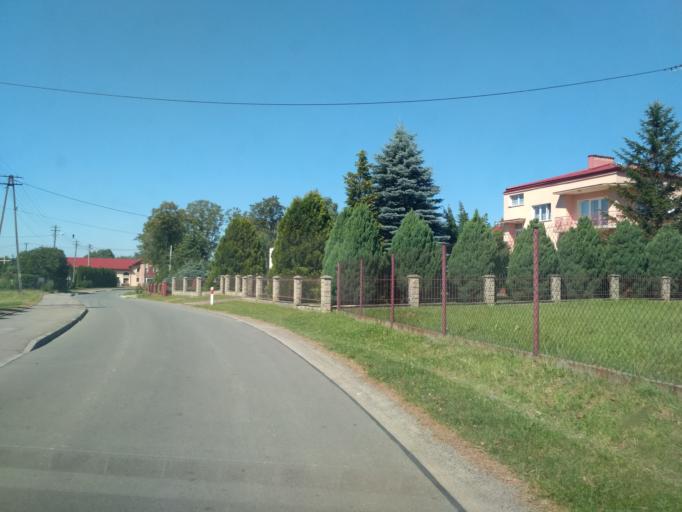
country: PL
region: Subcarpathian Voivodeship
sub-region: Powiat krosnienski
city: Miejsce Piastowe
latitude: 49.6294
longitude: 21.7365
